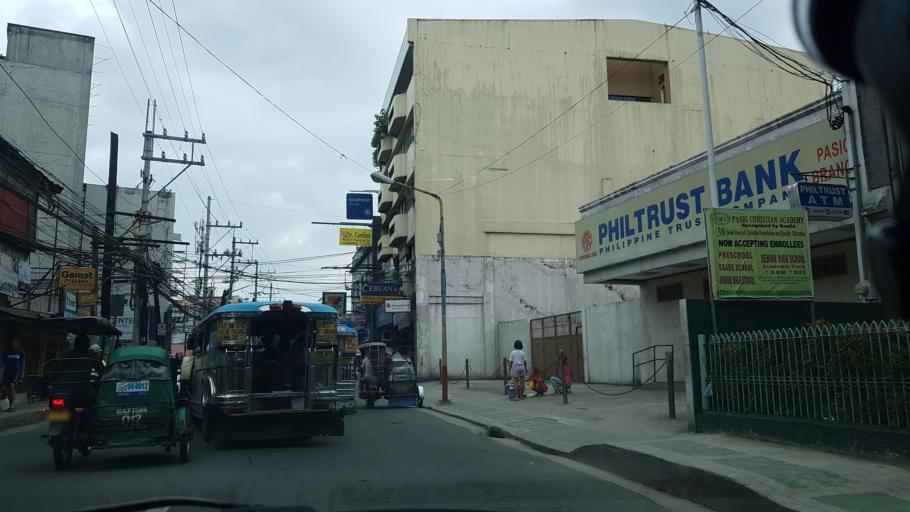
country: PH
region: Metro Manila
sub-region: Pasig
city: Pasig City
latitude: 14.5667
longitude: 121.0762
